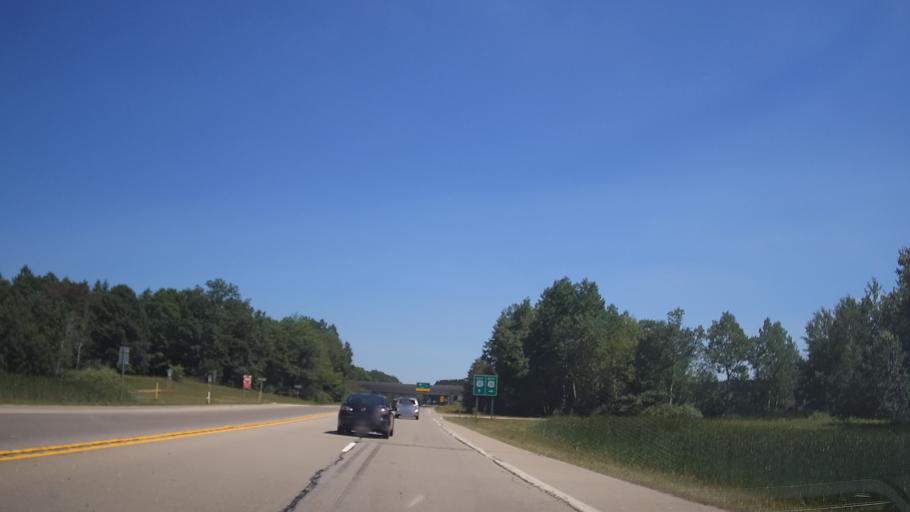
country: US
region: Michigan
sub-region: Clare County
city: Clare
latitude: 43.8669
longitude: -84.9136
